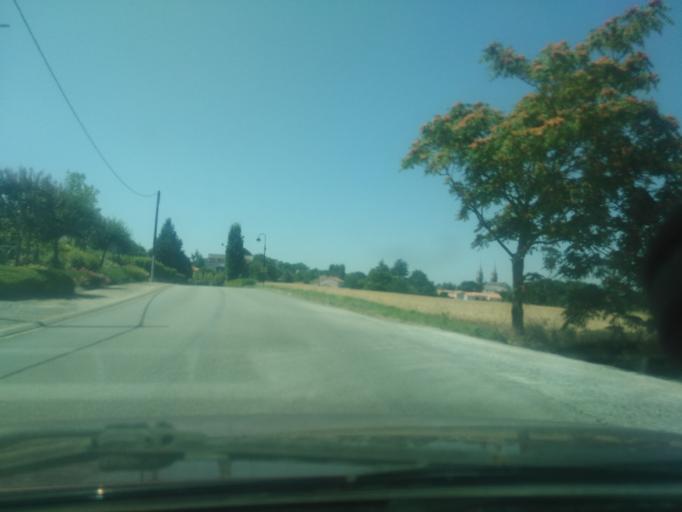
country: FR
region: Pays de la Loire
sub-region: Departement de la Vendee
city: Les Essarts
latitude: 46.7695
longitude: -1.2209
